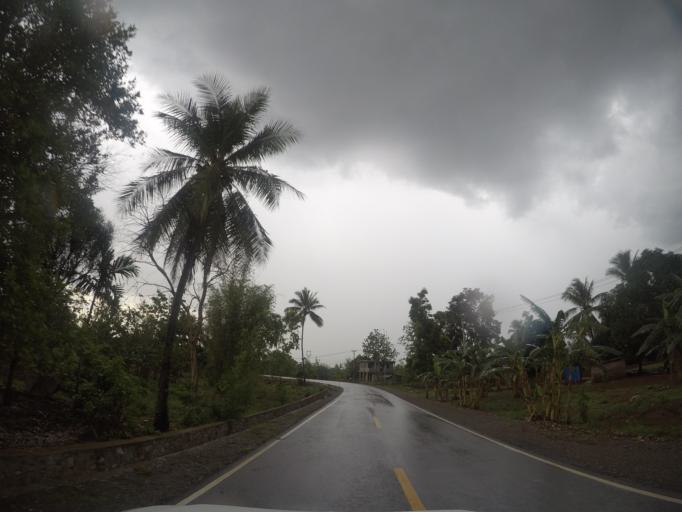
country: TL
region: Bobonaro
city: Maliana
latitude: -8.9492
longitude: 125.2077
